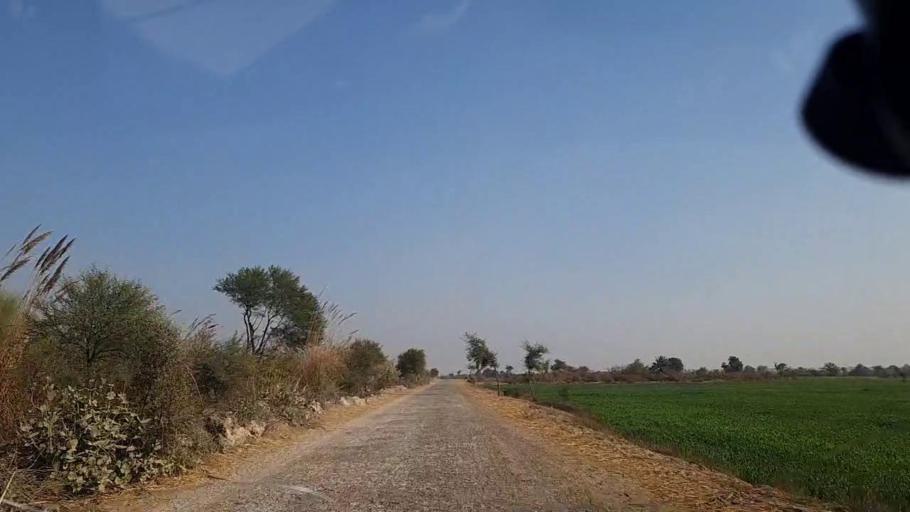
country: PK
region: Sindh
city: Khanpur
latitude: 27.6844
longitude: 69.5283
